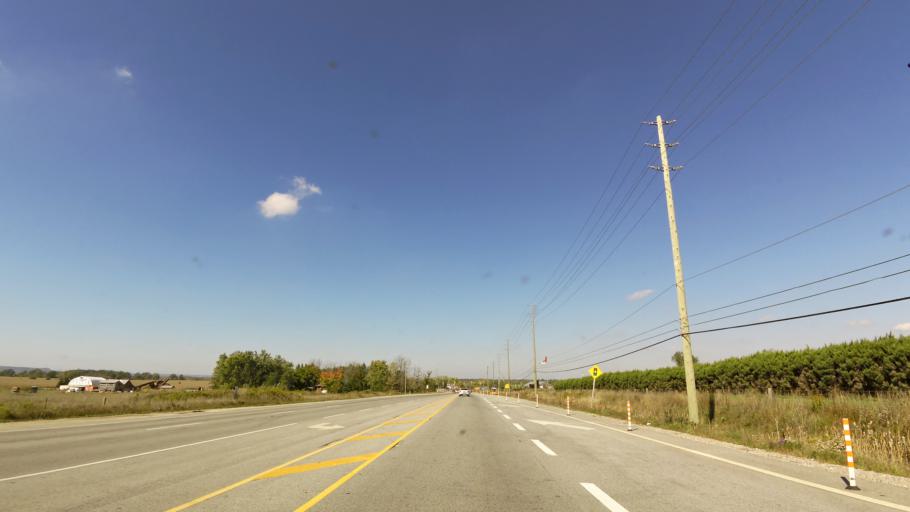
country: CA
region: Ontario
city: Burlington
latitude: 43.4636
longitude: -79.8067
